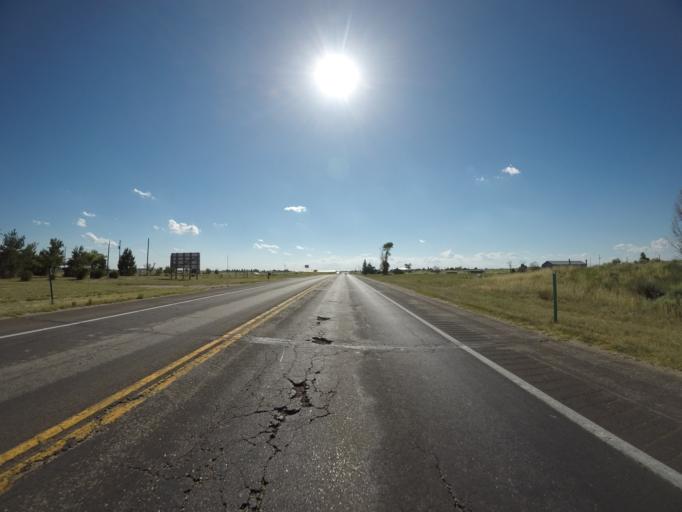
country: US
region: Colorado
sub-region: Logan County
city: Sterling
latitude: 40.6236
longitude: -103.2691
